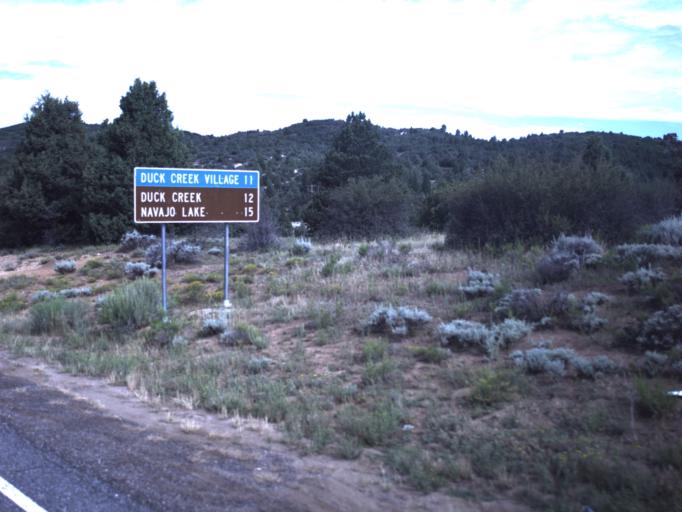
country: US
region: Utah
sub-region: Garfield County
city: Panguitch
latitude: 37.4895
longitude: -112.5175
